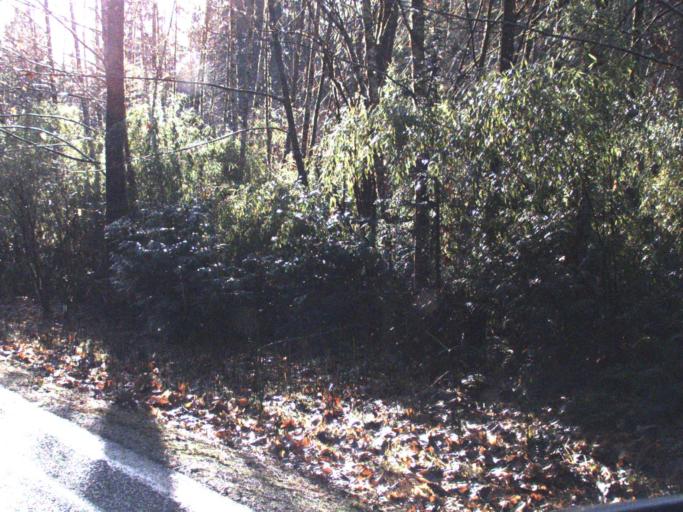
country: US
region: Washington
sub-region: Snohomish County
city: Darrington
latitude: 48.4455
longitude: -121.5825
